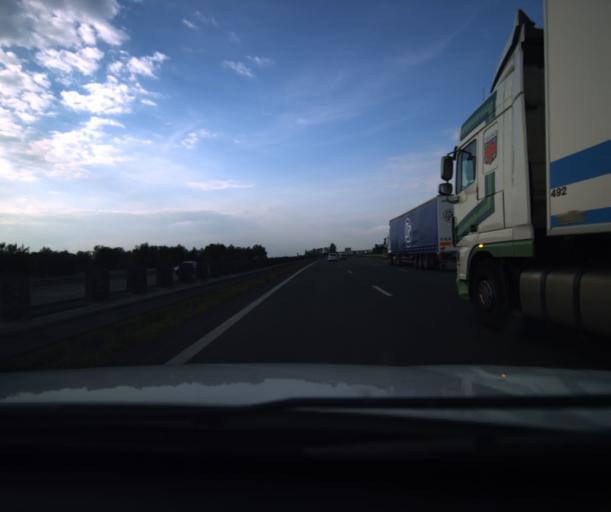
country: FR
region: Midi-Pyrenees
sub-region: Departement du Tarn-et-Garonne
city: Grisolles
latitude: 43.8547
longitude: 1.3187
